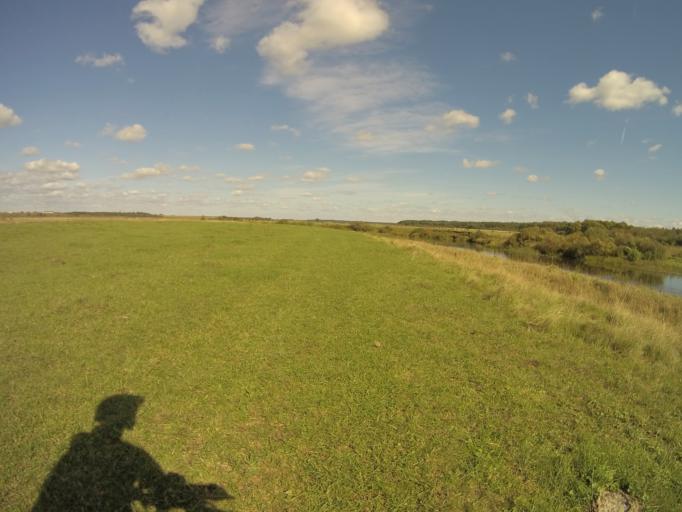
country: RU
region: Vladimir
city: Orgtrud
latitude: 56.2971
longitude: 40.6192
